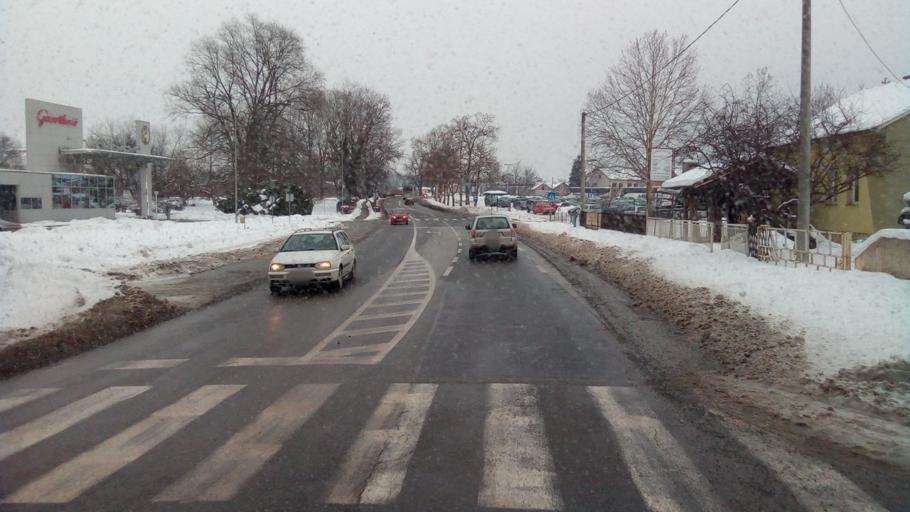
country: HR
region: Sisacko-Moslavacka
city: Petrinja
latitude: 45.4416
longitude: 16.2906
